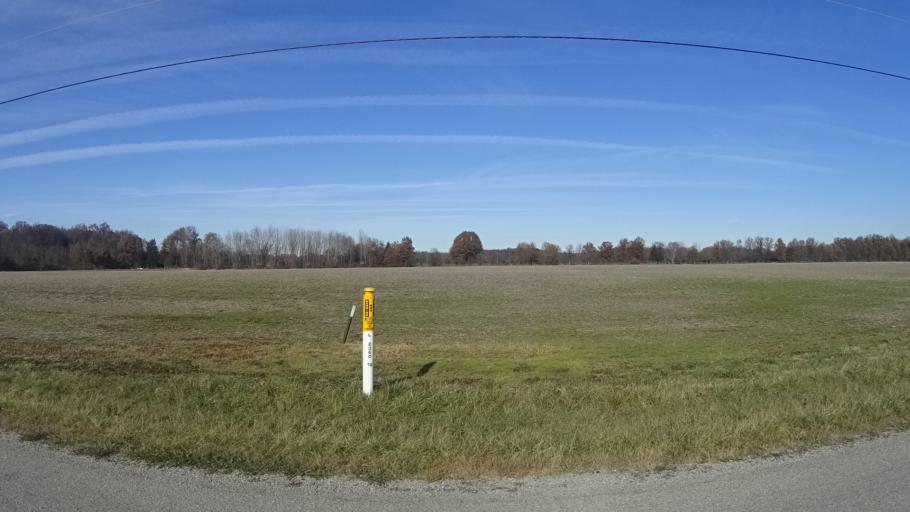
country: US
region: Ohio
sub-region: Lorain County
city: Eaton Estates
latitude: 41.3405
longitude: -81.9884
